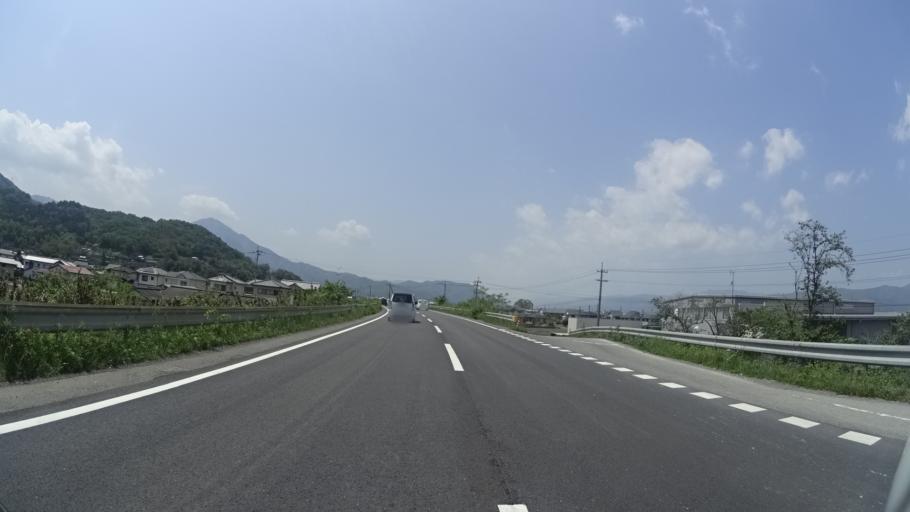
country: JP
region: Tokushima
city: Kamojimacho-jogejima
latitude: 34.0625
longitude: 134.2581
